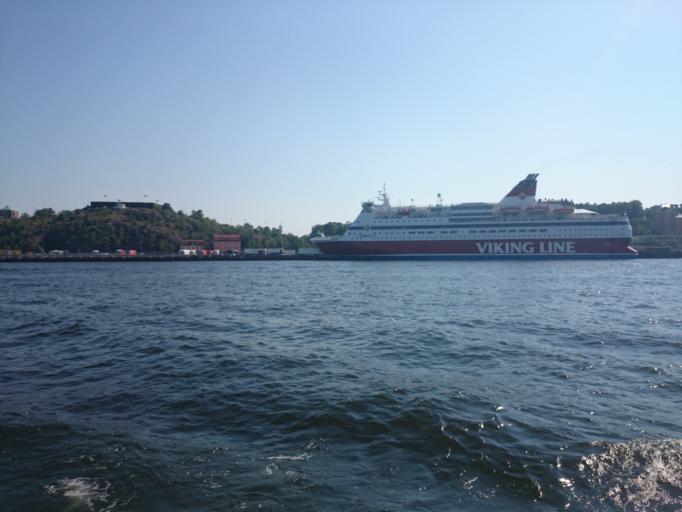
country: SE
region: Stockholm
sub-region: Stockholms Kommun
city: OEstermalm
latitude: 59.3189
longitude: 18.0997
